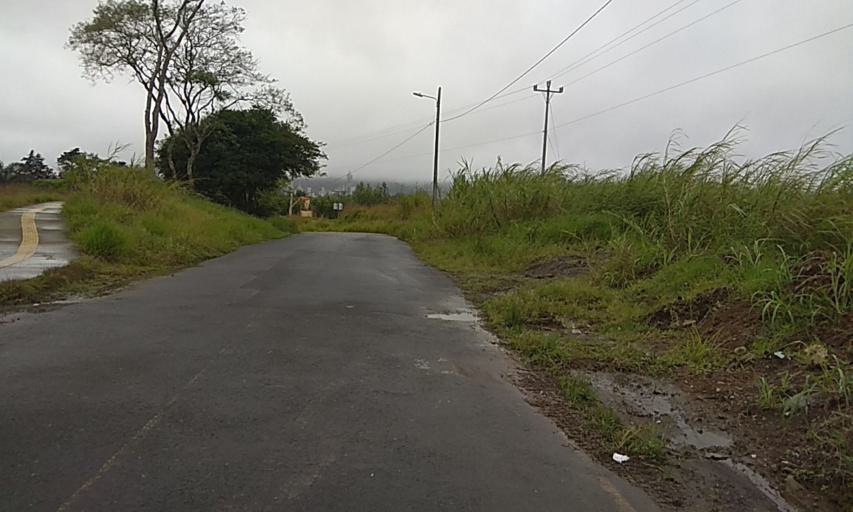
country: CR
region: Cartago
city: Cartago
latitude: 9.8511
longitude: -83.9120
